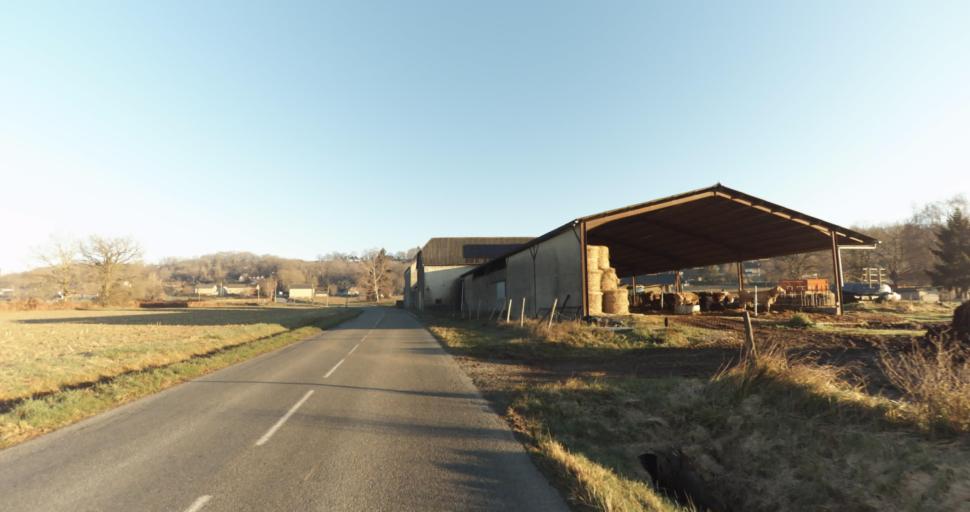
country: FR
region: Aquitaine
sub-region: Departement des Pyrenees-Atlantiques
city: Morlaas
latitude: 43.3243
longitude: -0.2734
